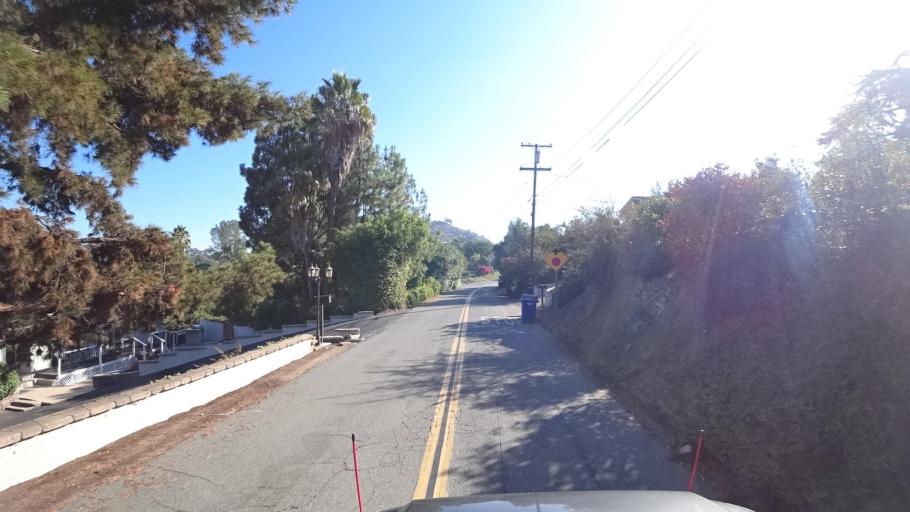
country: US
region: California
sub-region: San Diego County
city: Spring Valley
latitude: 32.7621
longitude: -116.9955
